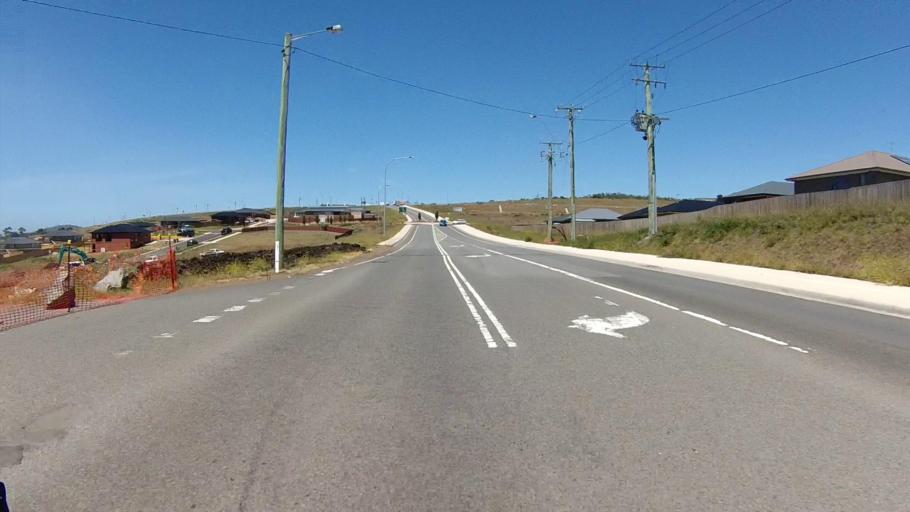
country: AU
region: Tasmania
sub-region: Clarence
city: Howrah
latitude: -42.8850
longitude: 147.4285
